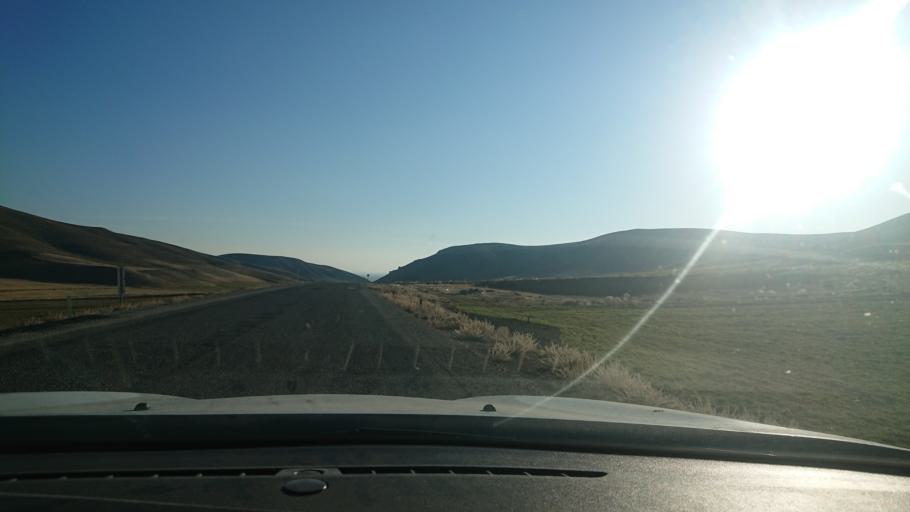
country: TR
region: Aksaray
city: Acipinar
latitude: 38.7016
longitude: 33.7535
